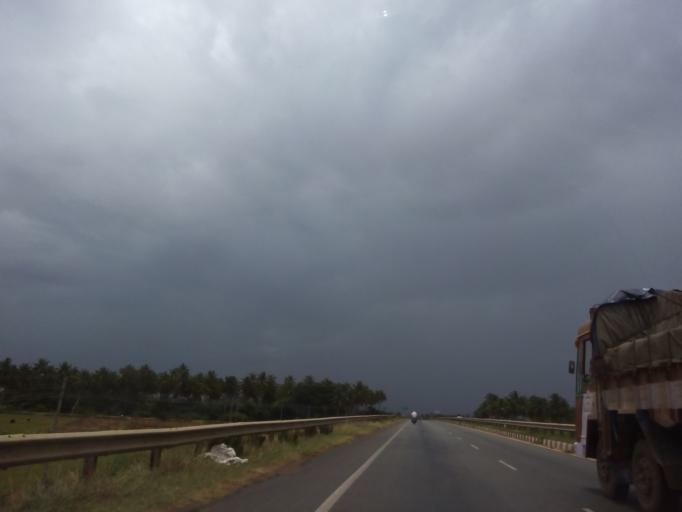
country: IN
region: Karnataka
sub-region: Davanagere
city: Harihar
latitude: 14.4523
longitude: 75.8741
